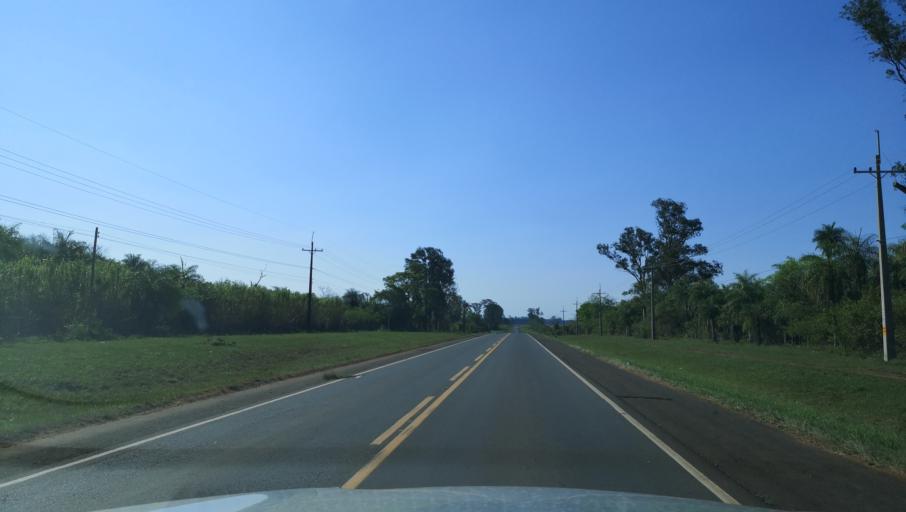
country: PY
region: Misiones
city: San Patricio
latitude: -26.9479
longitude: -56.8467
